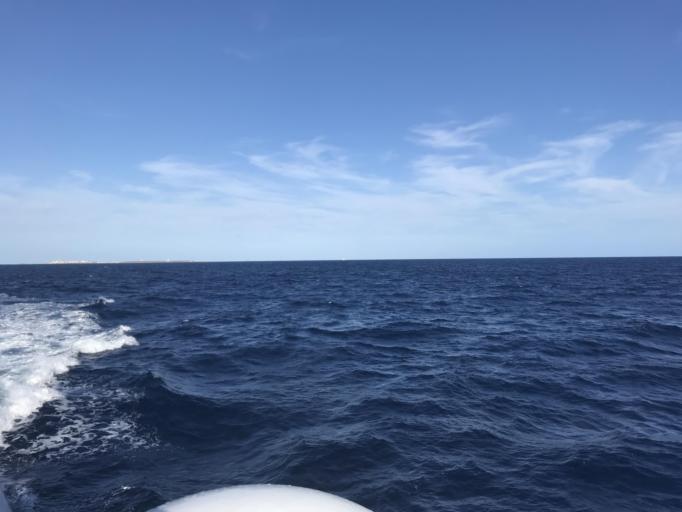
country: ES
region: Valencia
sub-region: Provincia de Alicante
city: Santa Pola
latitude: 38.1404
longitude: -0.5230
